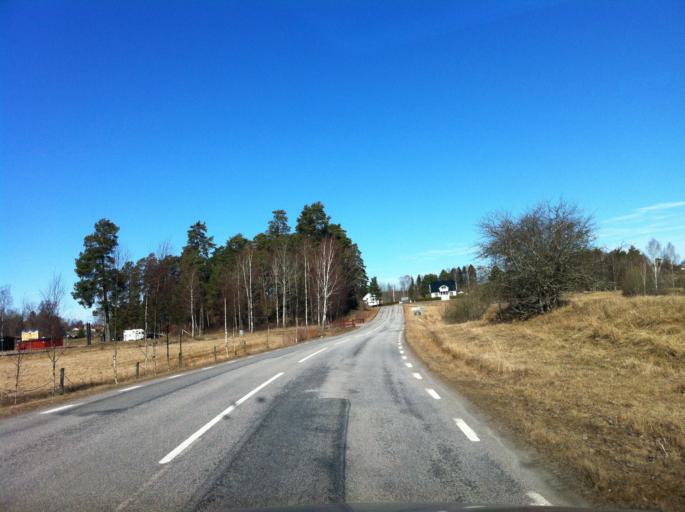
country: SE
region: Vaestra Goetaland
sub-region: Toreboda Kommun
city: Toereboda
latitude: 58.7115
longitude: 14.1311
